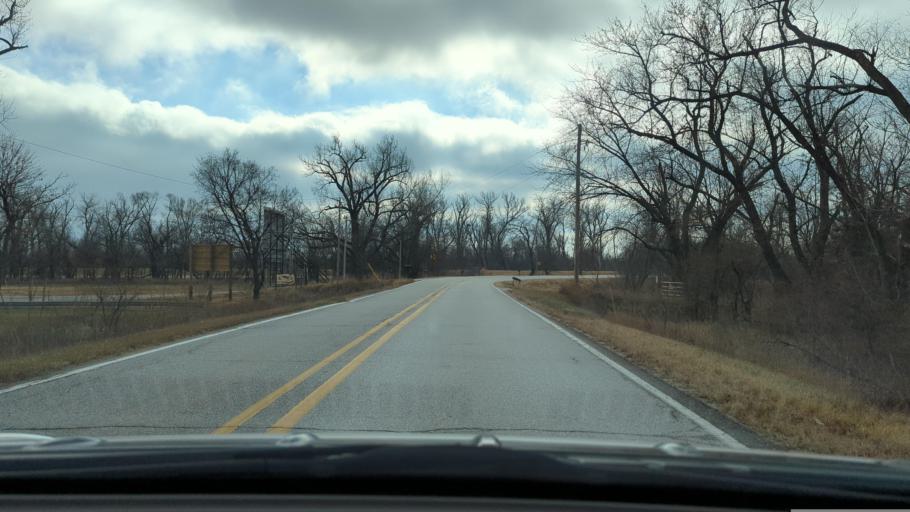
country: US
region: Nebraska
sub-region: Sarpy County
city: Offutt Air Force Base
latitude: 41.0657
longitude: -95.9232
